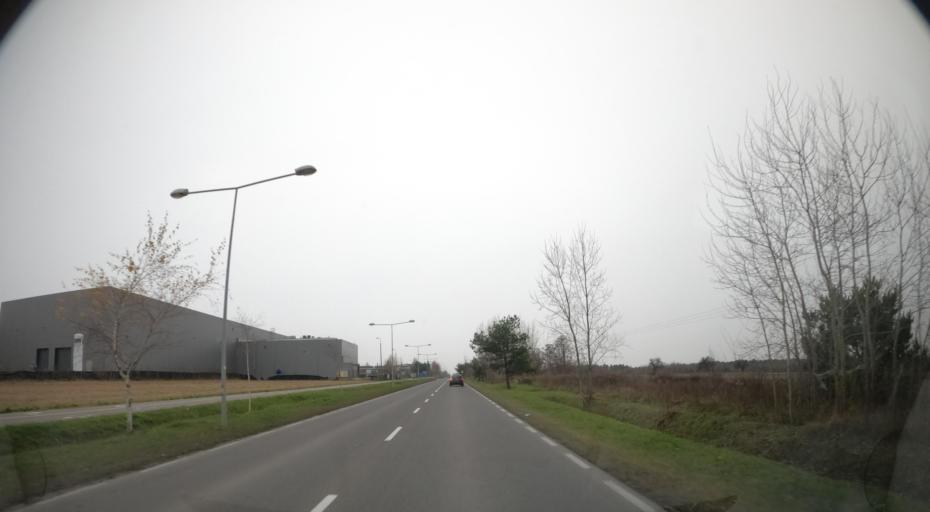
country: PL
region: Masovian Voivodeship
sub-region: Radom
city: Radom
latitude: 51.4480
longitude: 21.1927
